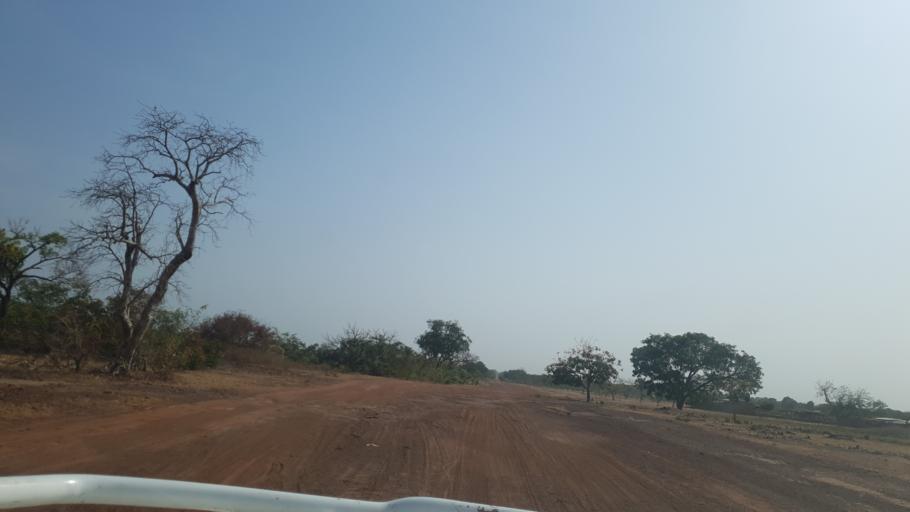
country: ML
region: Koulikoro
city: Dioila
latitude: 12.6680
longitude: -6.6909
